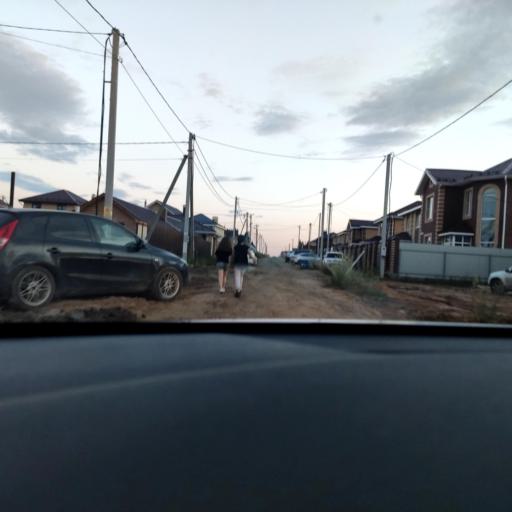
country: RU
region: Tatarstan
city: Stolbishchi
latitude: 55.7231
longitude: 49.3008
